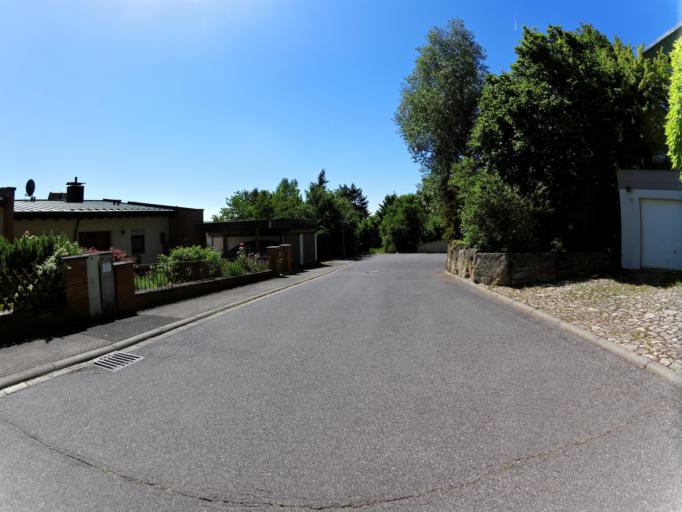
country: DE
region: Bavaria
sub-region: Regierungsbezirk Unterfranken
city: Ochsenfurt
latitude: 49.6740
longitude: 10.0558
